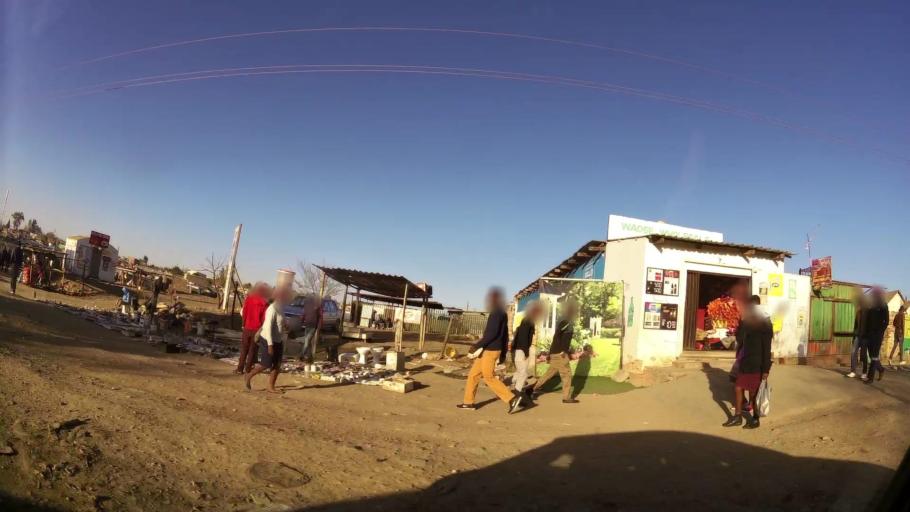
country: ZA
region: Gauteng
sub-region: City of Johannesburg Metropolitan Municipality
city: Diepsloot
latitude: -25.9327
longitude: 28.0147
